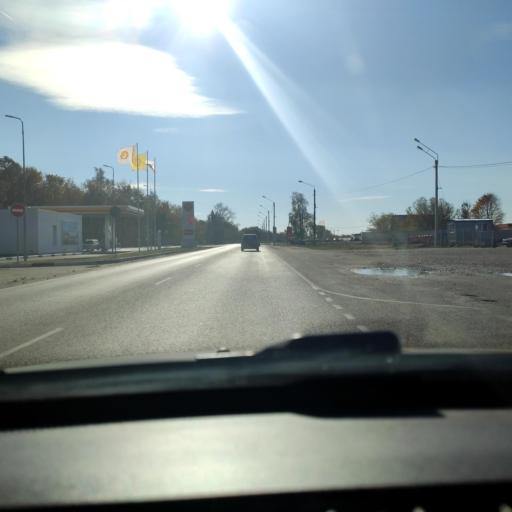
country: RU
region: Voronezj
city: Voronezh
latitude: 51.6176
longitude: 39.1771
